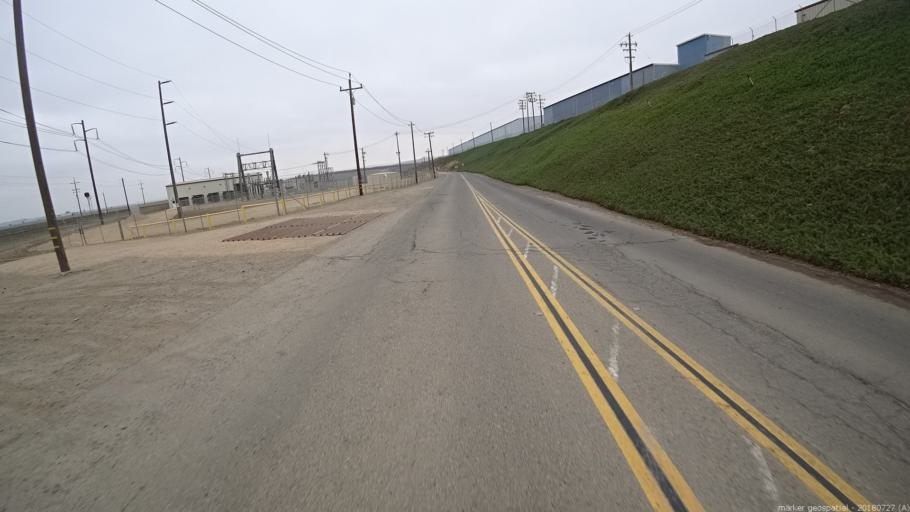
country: US
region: California
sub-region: Monterey County
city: King City
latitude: 36.2276
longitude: -121.1295
